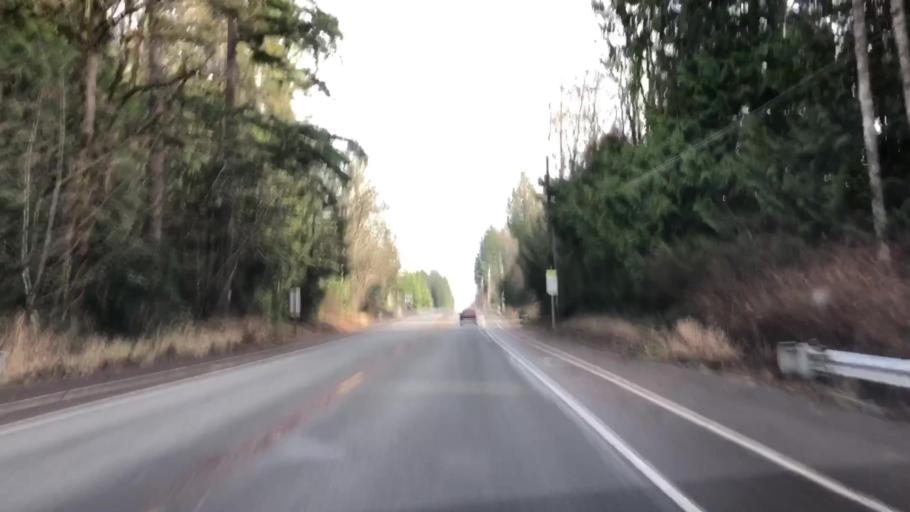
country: US
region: Washington
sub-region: Kitsap County
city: Kingston
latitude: 47.7949
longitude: -122.5288
